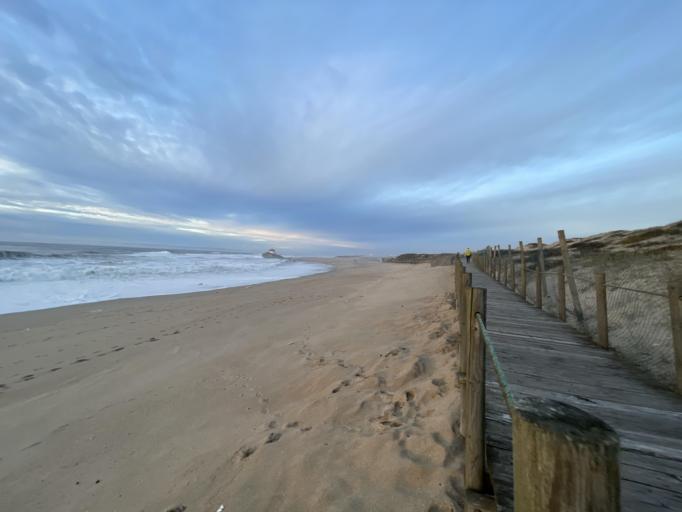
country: PT
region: Porto
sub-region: Vila Nova de Gaia
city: Vila Nova da Telha
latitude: 41.0648
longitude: -8.6567
